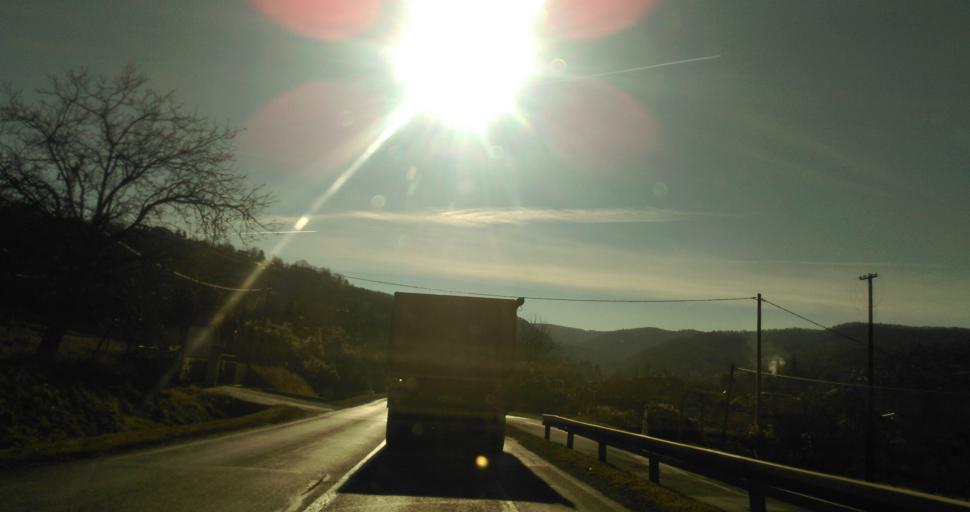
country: RS
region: Autonomna Pokrajina Vojvodina
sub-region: Juznobacki Okrug
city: Novi Sad
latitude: 45.2022
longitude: 19.8423
